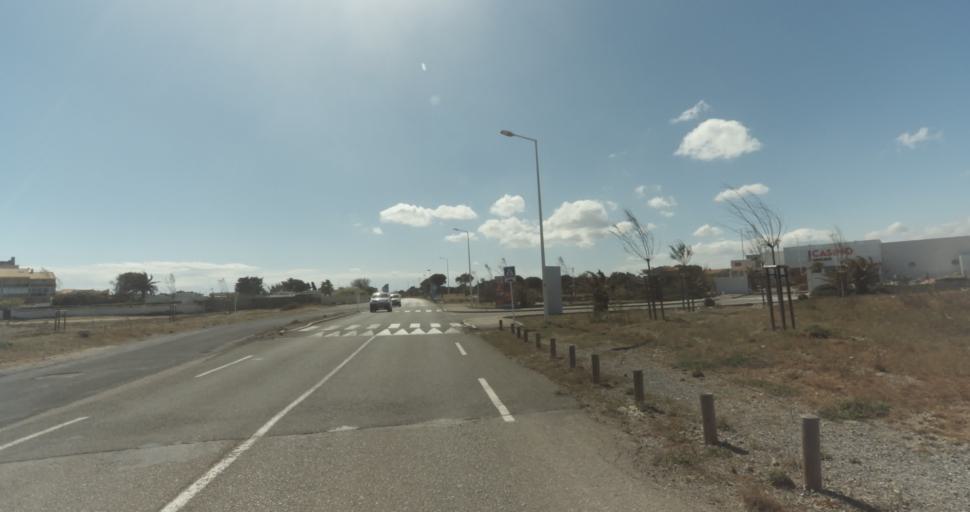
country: FR
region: Languedoc-Roussillon
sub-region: Departement des Pyrenees-Orientales
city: Le Barcares
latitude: 42.8401
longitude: 3.0418
